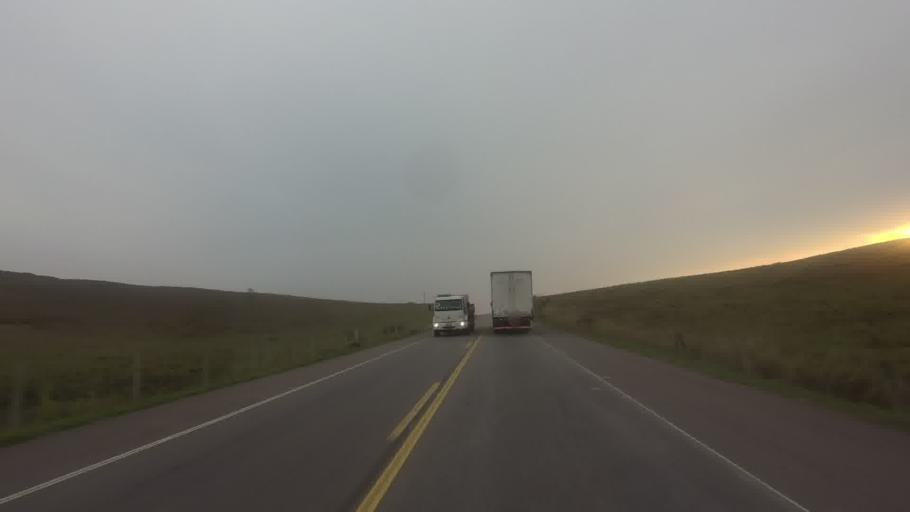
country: BR
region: Minas Gerais
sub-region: Recreio
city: Recreio
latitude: -21.6841
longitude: -42.4013
